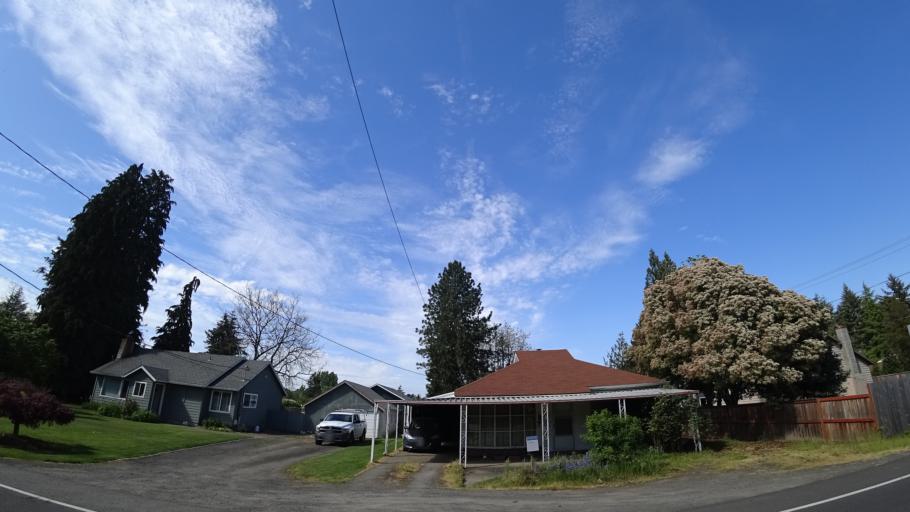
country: US
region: Oregon
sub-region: Washington County
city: Aloha
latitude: 45.5005
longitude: -122.8816
